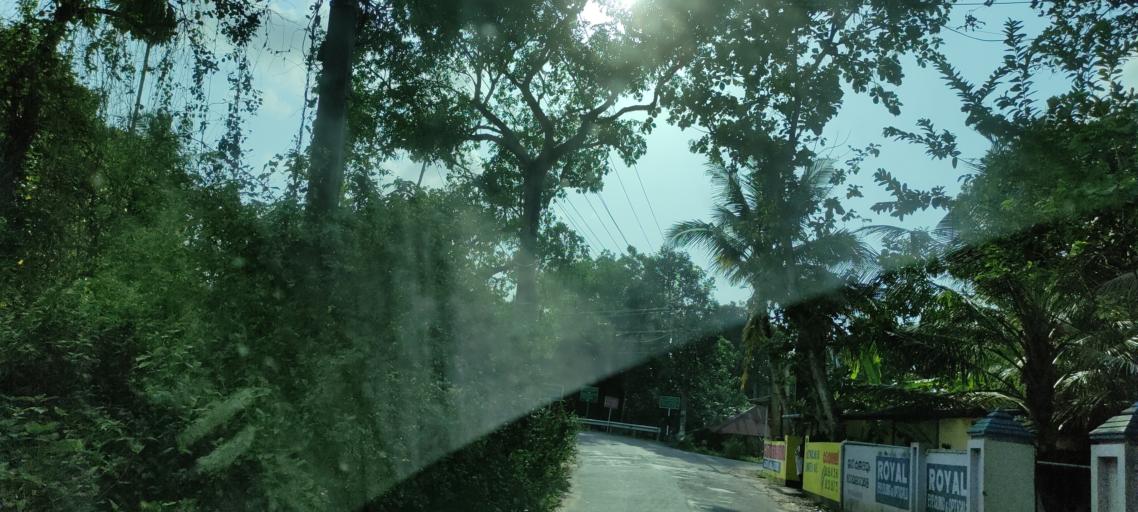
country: IN
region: Kerala
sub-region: Alappuzha
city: Vayalar
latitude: 9.6862
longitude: 76.3044
